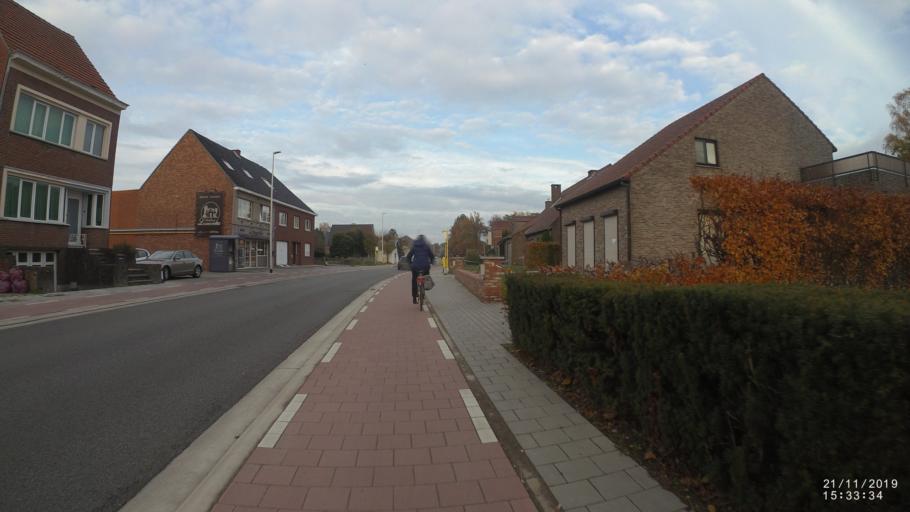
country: BE
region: Flanders
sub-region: Provincie Limburg
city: Hasselt
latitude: 50.9472
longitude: 5.3084
